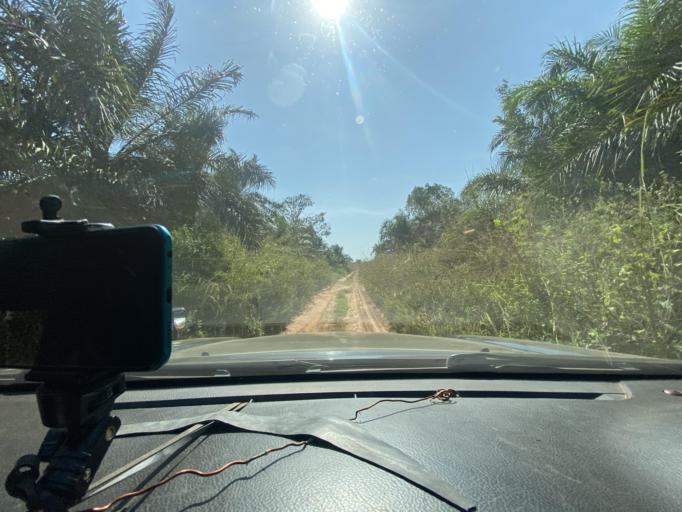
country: CD
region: Kasai-Oriental
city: Kabinda
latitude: -6.0979
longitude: 24.5390
